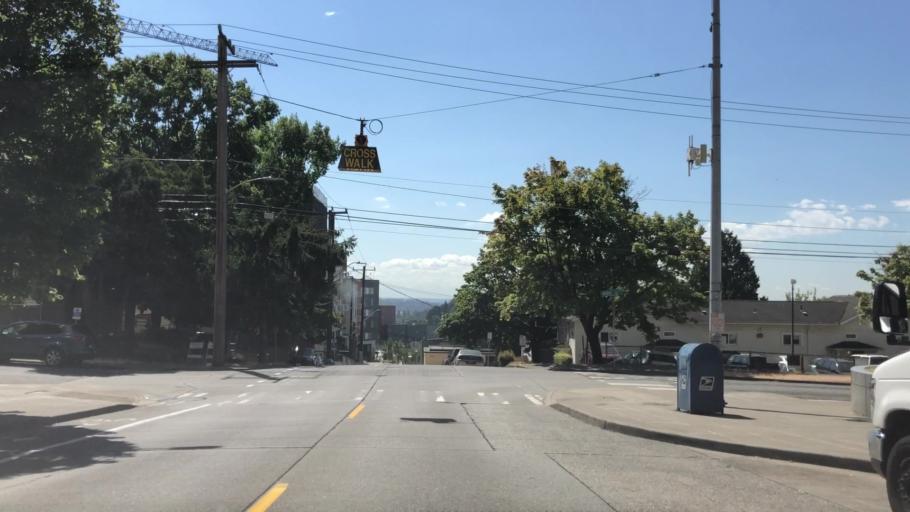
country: US
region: Washington
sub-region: King County
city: Seattle
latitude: 47.6036
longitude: -122.3230
